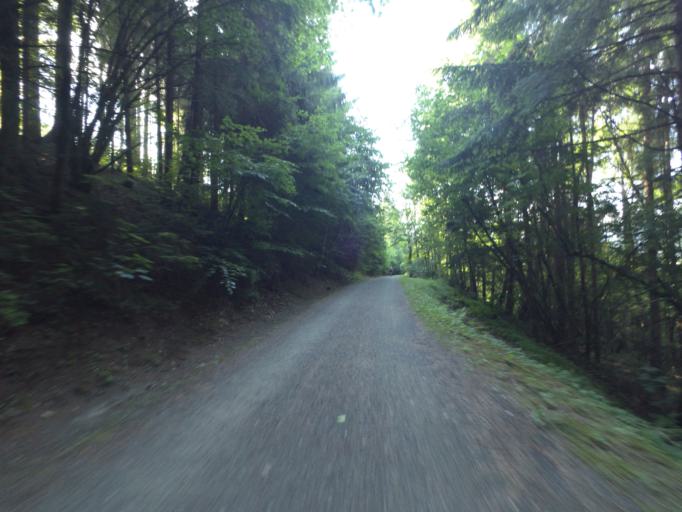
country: AT
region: Carinthia
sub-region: Politischer Bezirk Spittal an der Drau
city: Millstatt
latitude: 46.8013
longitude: 13.5473
